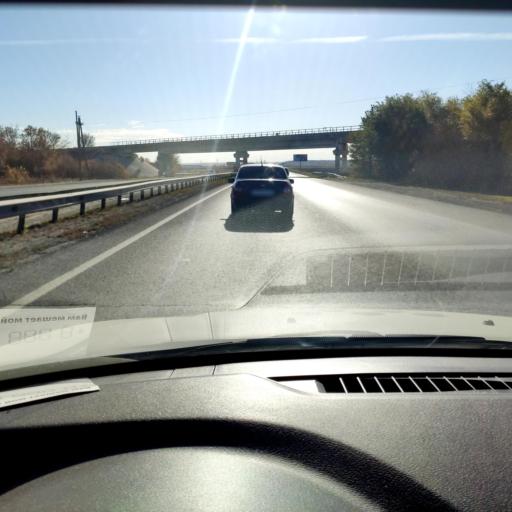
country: RU
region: Samara
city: Tol'yatti
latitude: 53.5638
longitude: 49.4962
